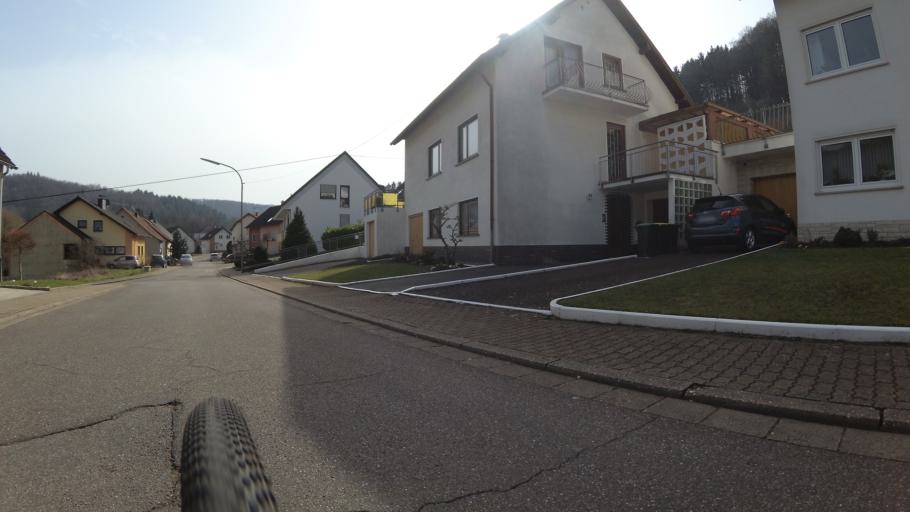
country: DE
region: Saarland
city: Beckingen
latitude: 49.4296
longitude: 6.7267
